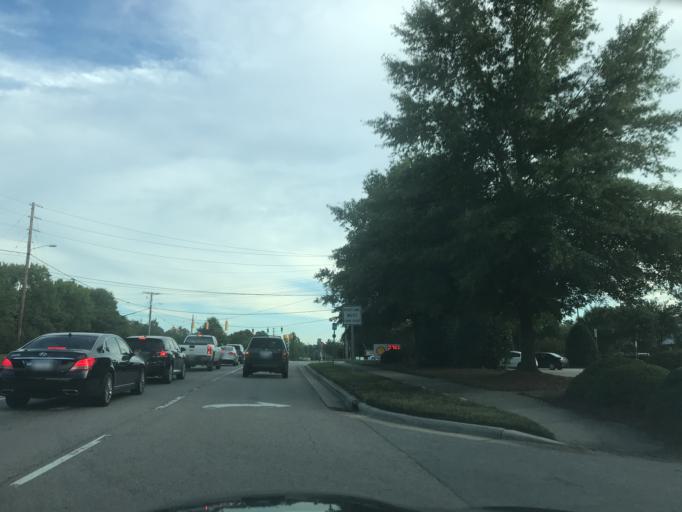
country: US
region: North Carolina
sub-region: Wake County
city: Apex
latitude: 35.7366
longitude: -78.8633
